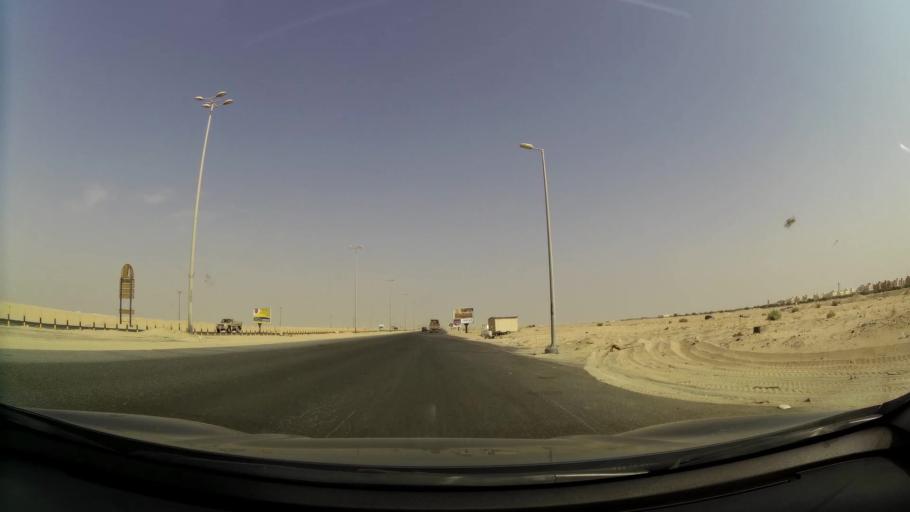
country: KW
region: Al Ahmadi
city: Al Wafrah
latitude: 28.8073
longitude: 48.0412
